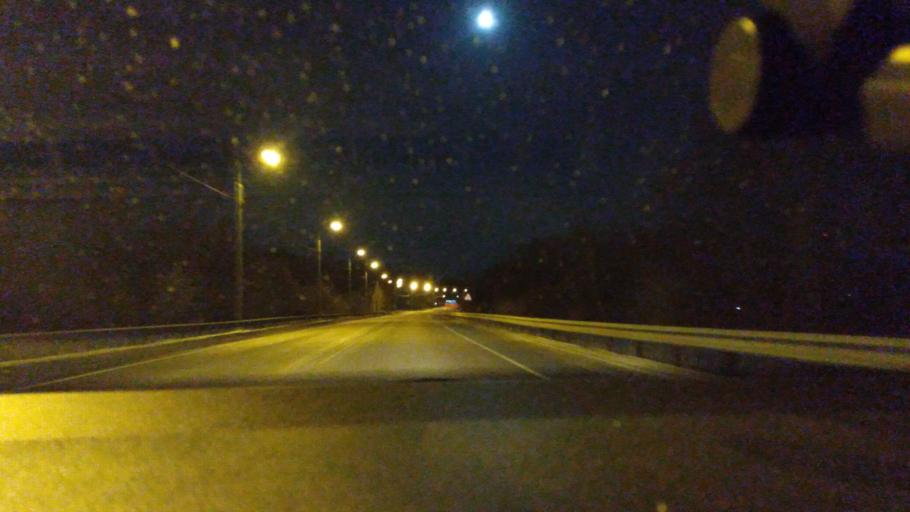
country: RU
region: Moskovskaya
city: Il'inskiy Pogost
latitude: 55.4872
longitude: 38.9109
